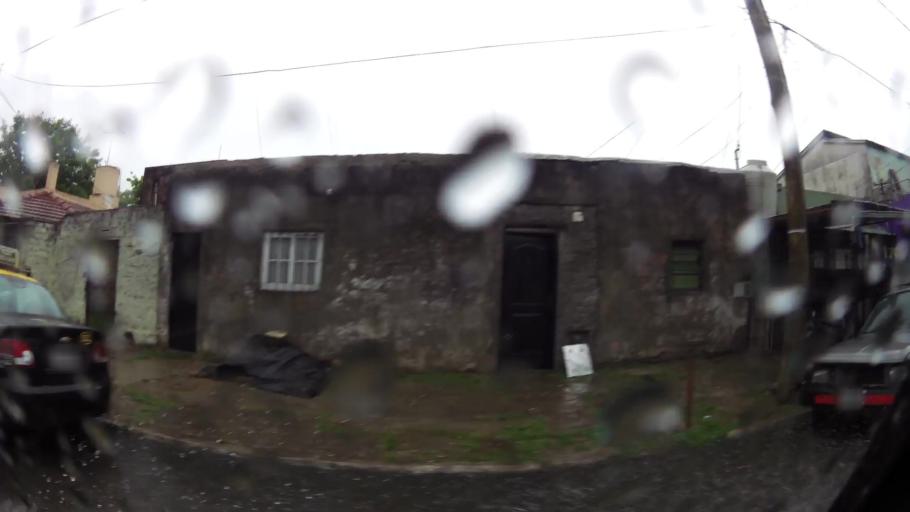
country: AR
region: Buenos Aires
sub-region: Partido de Lanus
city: Lanus
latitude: -34.7200
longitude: -58.4078
